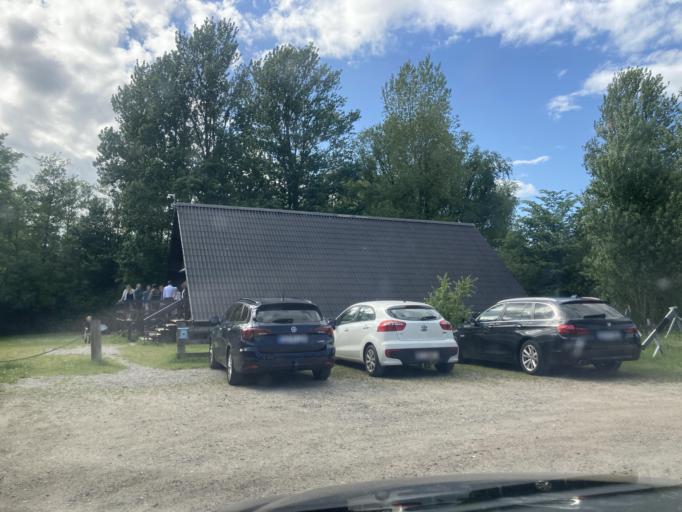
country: DK
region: Capital Region
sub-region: Gribskov Kommune
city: Helsinge
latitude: 56.0020
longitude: 12.1102
